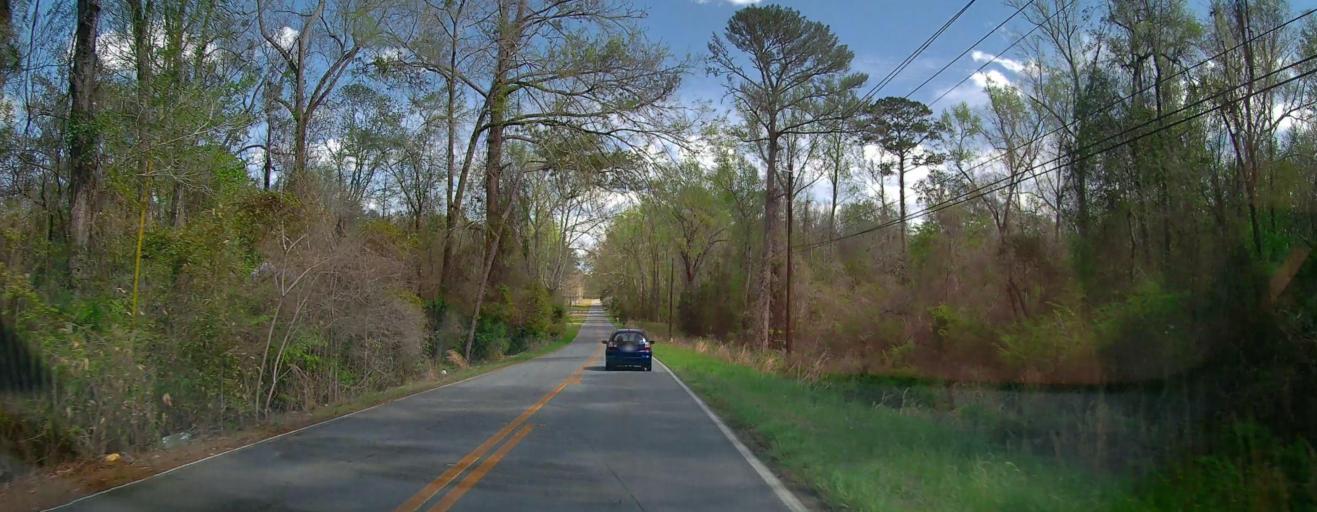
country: US
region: Georgia
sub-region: Bibb County
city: Macon
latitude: 32.8179
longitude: -83.5508
